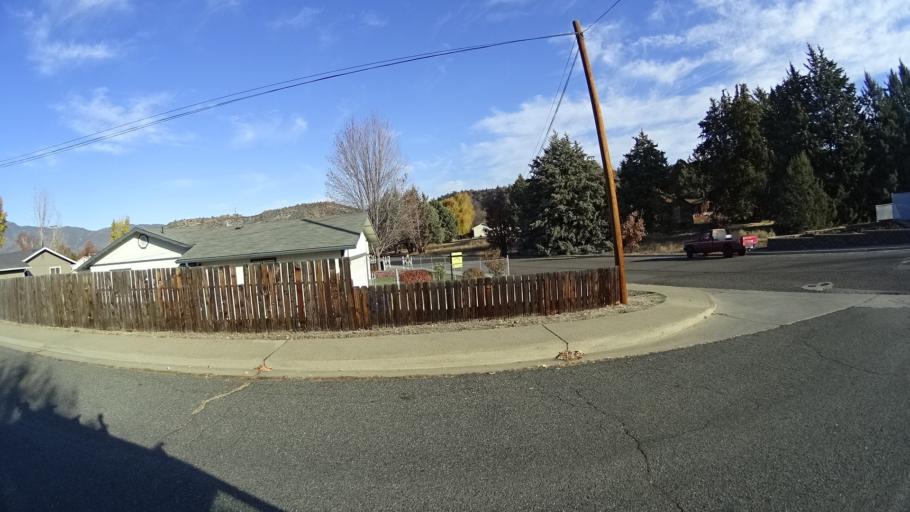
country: US
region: California
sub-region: Siskiyou County
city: Yreka
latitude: 41.7112
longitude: -122.6220
